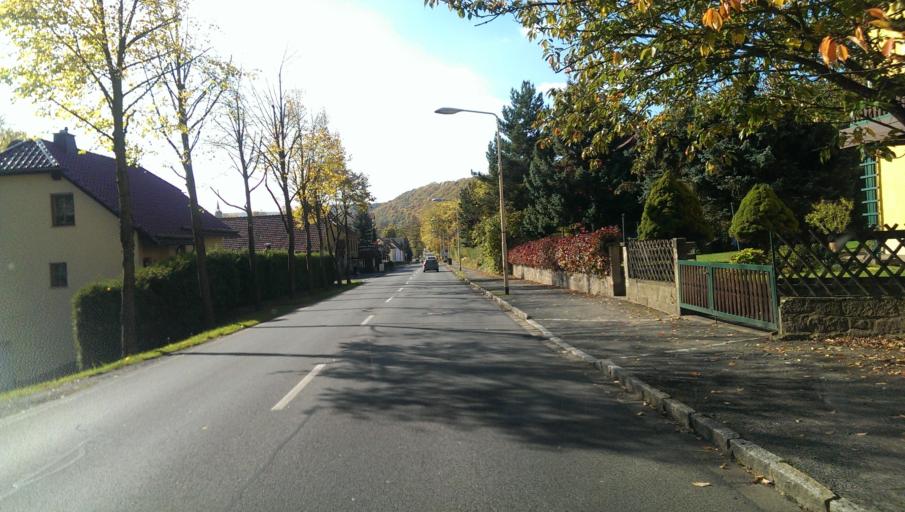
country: DE
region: Saxony
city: Dohma
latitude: 50.8778
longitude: 13.9508
